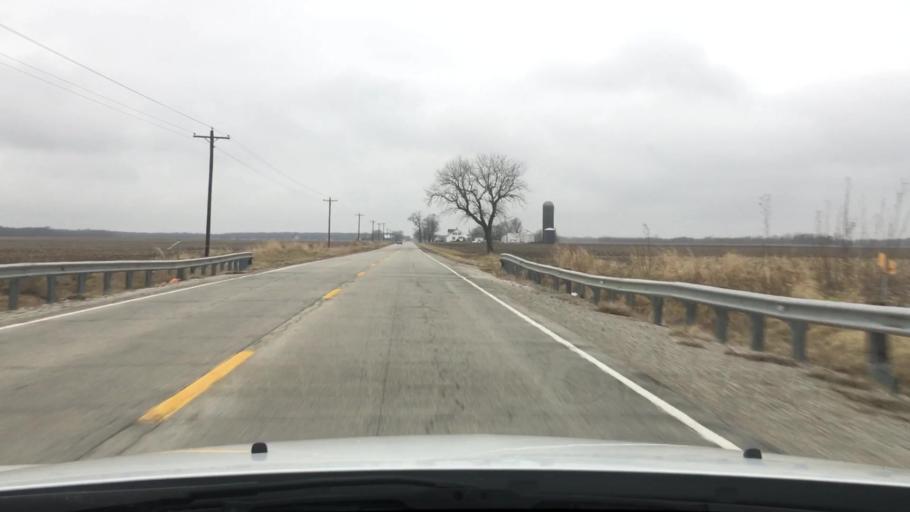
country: US
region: Illinois
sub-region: Iroquois County
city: Watseka
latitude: 40.8886
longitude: -87.7973
